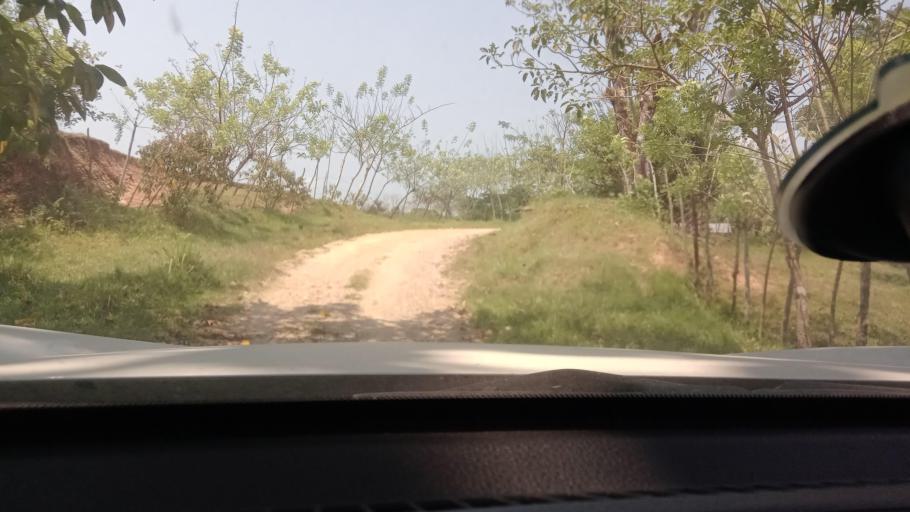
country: MX
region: Tabasco
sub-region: Huimanguillo
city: Francisco Rueda
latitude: 17.4847
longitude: -93.9374
